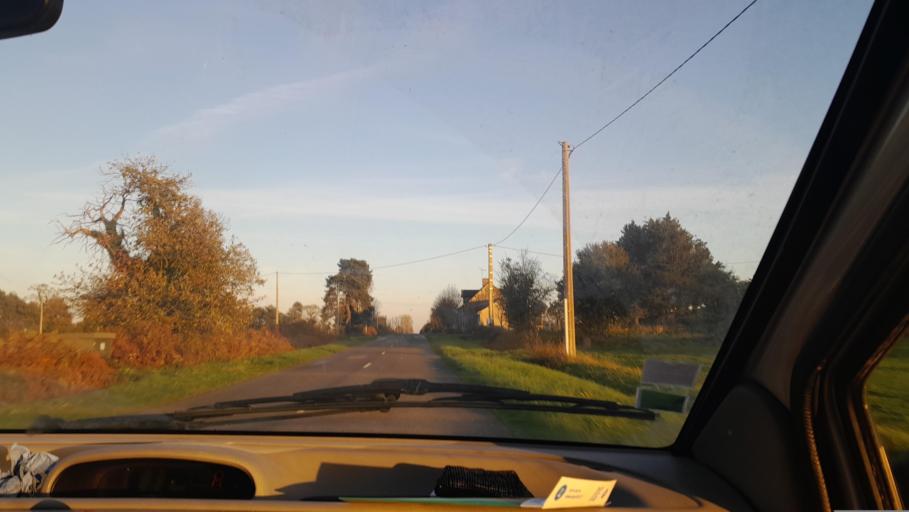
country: FR
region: Brittany
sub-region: Departement d'Ille-et-Vilaine
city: Le Pertre
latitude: 47.9676
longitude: -1.0730
